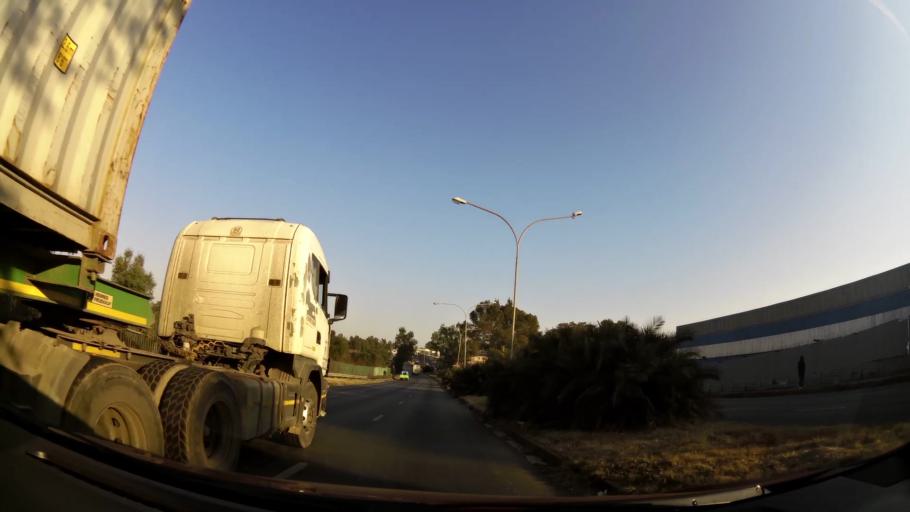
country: ZA
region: Gauteng
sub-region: City of Johannesburg Metropolitan Municipality
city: Johannesburg
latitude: -26.2108
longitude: 27.9937
